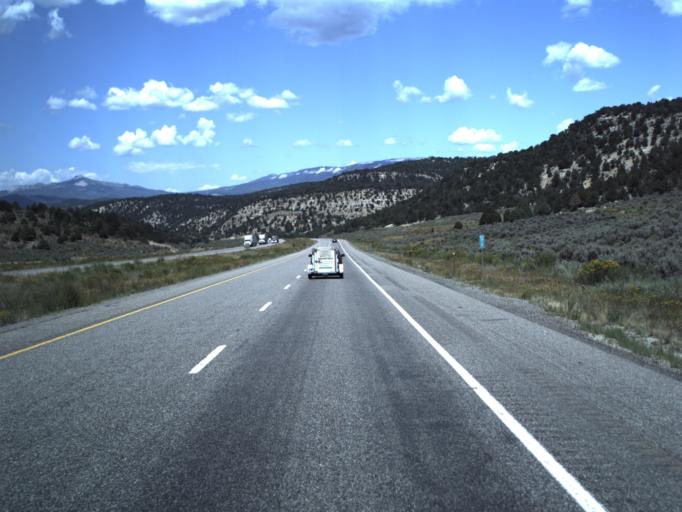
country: US
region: Utah
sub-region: Sevier County
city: Salina
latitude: 38.8289
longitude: -111.5387
